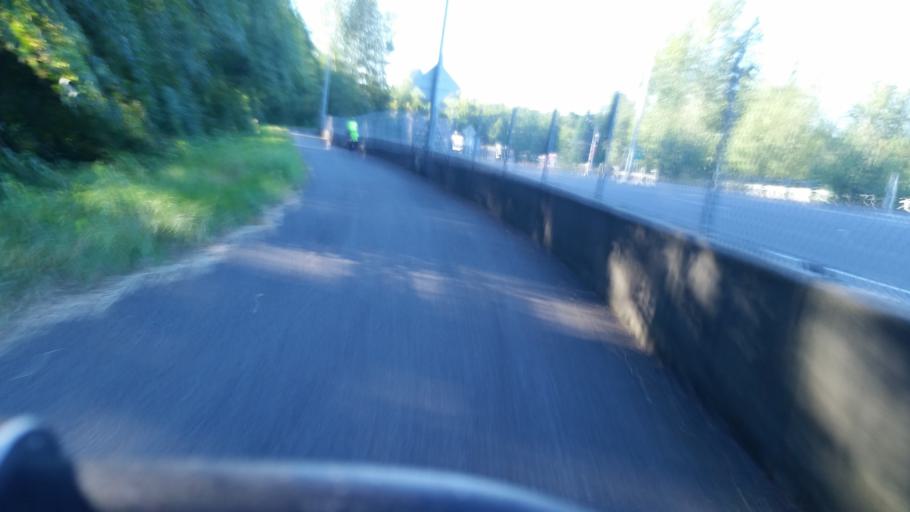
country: US
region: Washington
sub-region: King County
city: Redmond
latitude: 47.6676
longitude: -122.1293
